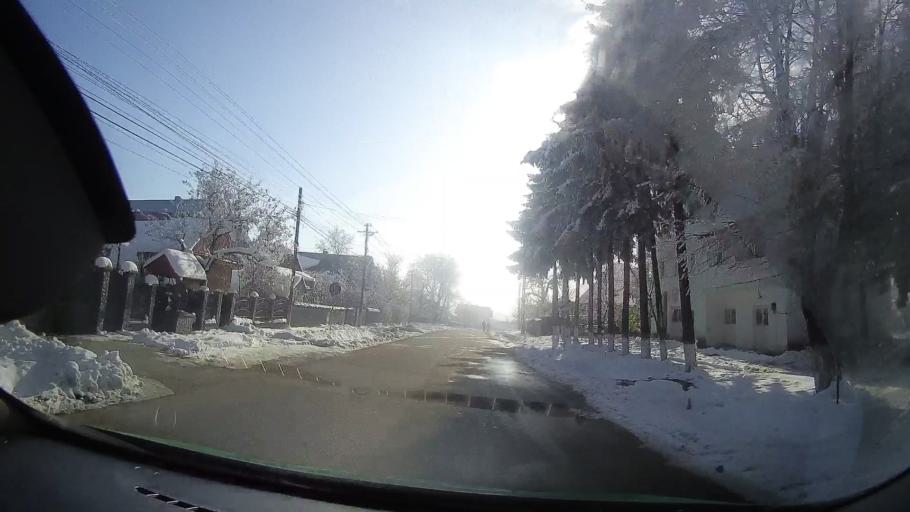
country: RO
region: Iasi
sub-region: Comuna Cristesti
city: Cristesti
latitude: 47.2586
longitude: 26.5749
